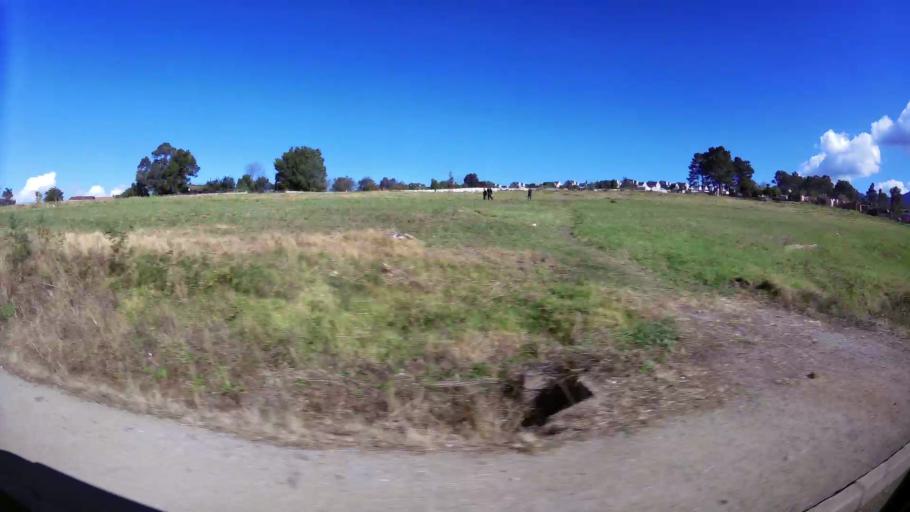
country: ZA
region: Western Cape
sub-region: Eden District Municipality
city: George
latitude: -33.9421
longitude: 22.4113
